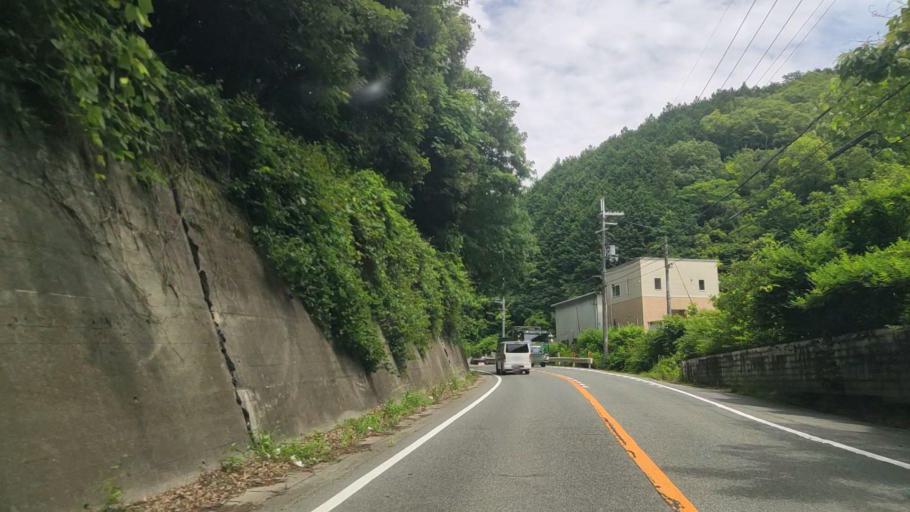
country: JP
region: Hyogo
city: Yamazakicho-nakabirose
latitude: 34.9911
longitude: 134.4047
